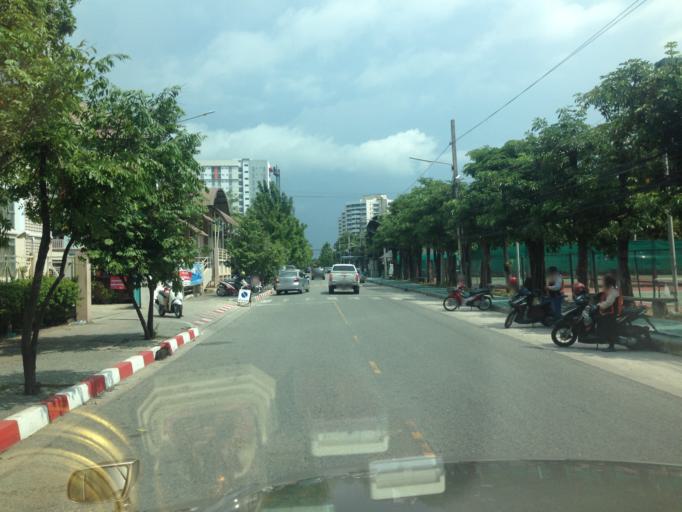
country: TH
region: Chon Buri
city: Chon Buri
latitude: 13.2769
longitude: 100.9280
